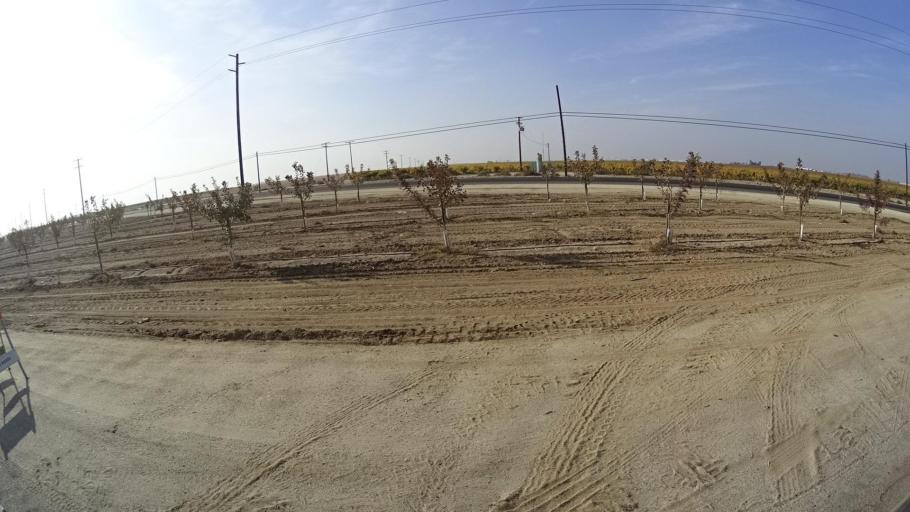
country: US
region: California
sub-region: Tulare County
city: Richgrove
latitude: 35.7874
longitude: -119.1163
